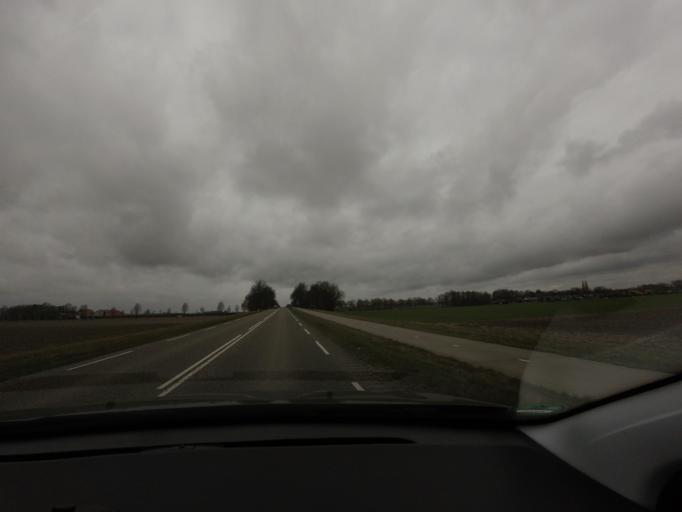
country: NL
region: Flevoland
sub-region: Gemeente Noordoostpolder
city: Emmeloord
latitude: 52.6943
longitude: 5.7294
